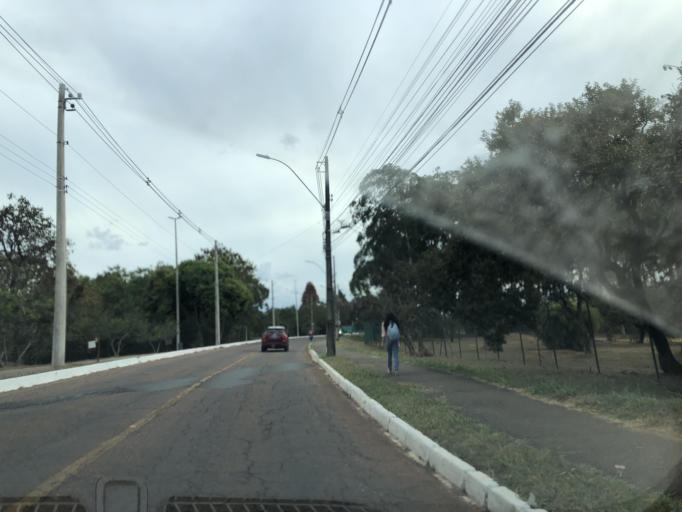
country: BR
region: Federal District
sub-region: Brasilia
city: Brasilia
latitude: -15.8821
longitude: -47.9628
